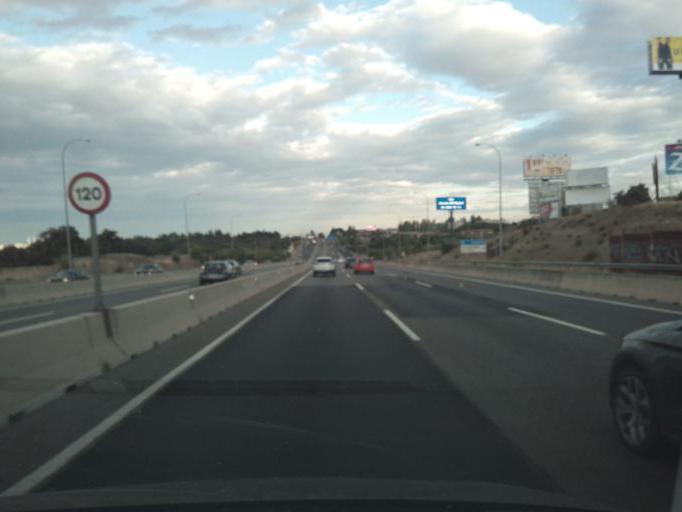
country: ES
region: Madrid
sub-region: Provincia de Madrid
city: Majadahonda
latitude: 40.4792
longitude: -3.8480
